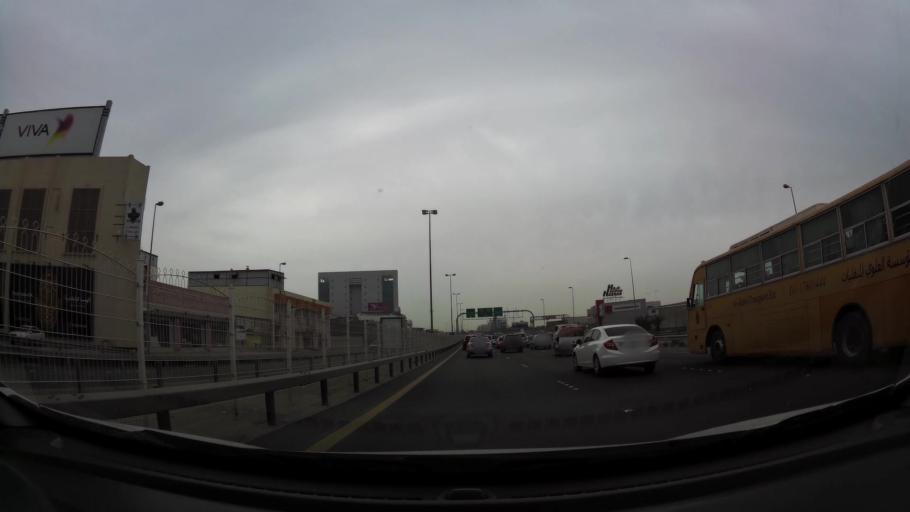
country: BH
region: Northern
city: Madinat `Isa
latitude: 26.1925
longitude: 50.5352
